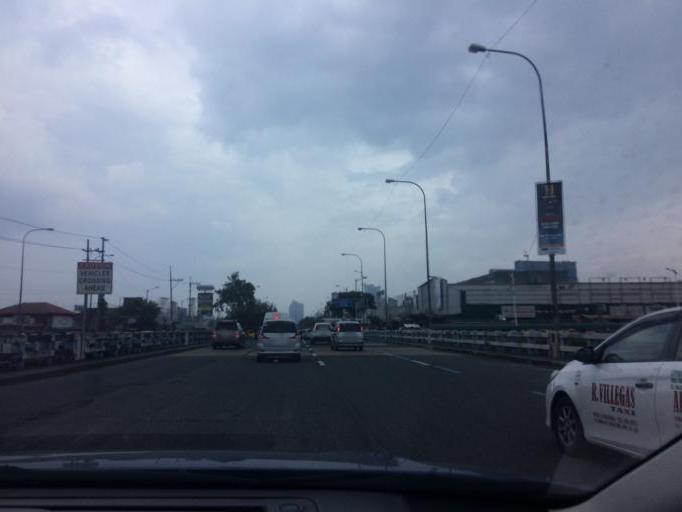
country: PH
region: Metro Manila
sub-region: City of Manila
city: Port Area
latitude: 14.5440
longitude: 120.9879
